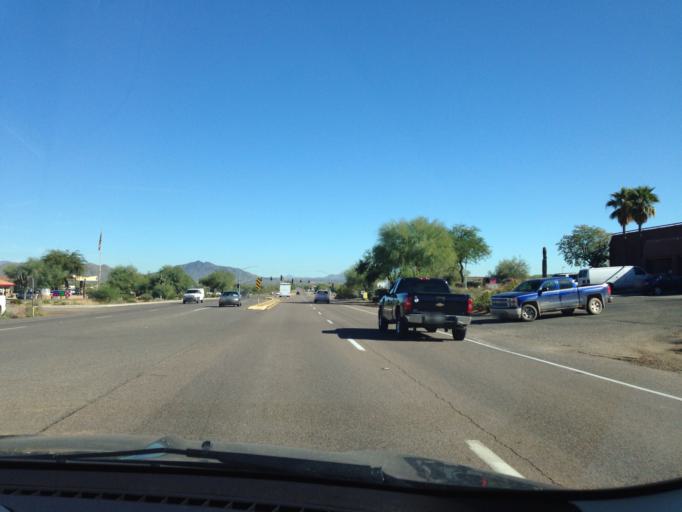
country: US
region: Arizona
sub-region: Maricopa County
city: Anthem
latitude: 33.7991
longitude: -112.0685
